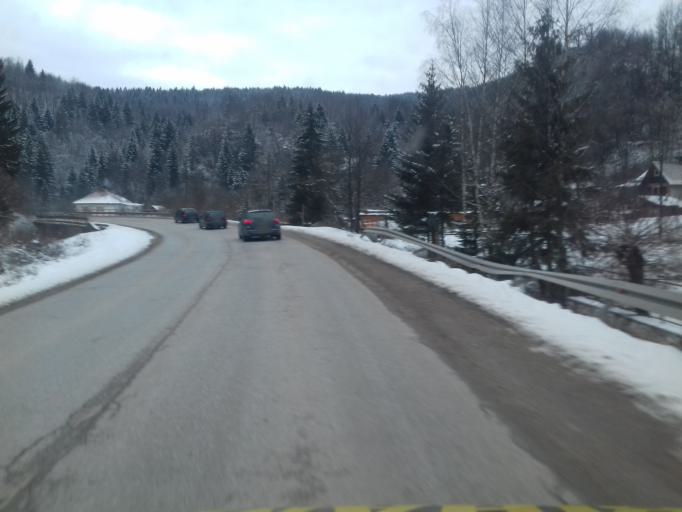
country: BA
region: Republika Srpska
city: Pale
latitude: 43.8650
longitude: 18.5485
